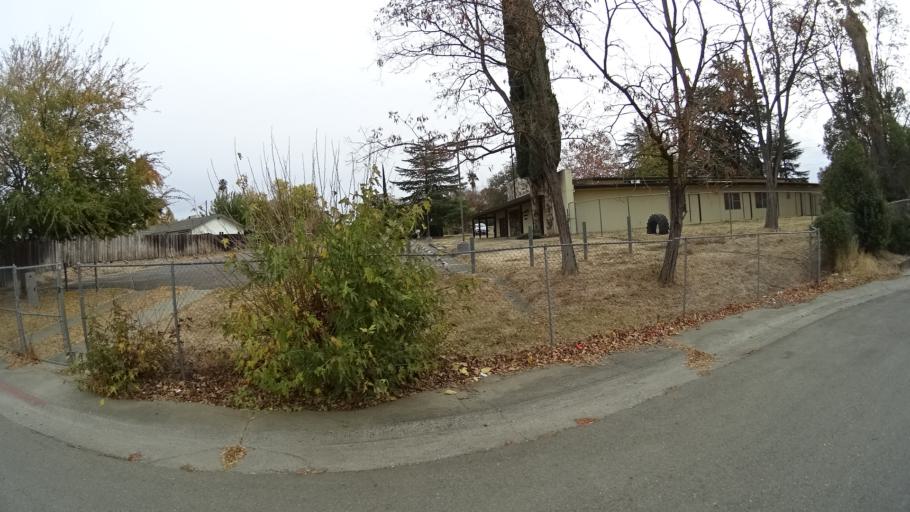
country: US
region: California
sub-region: Sacramento County
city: Citrus Heights
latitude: 38.7081
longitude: -121.3019
